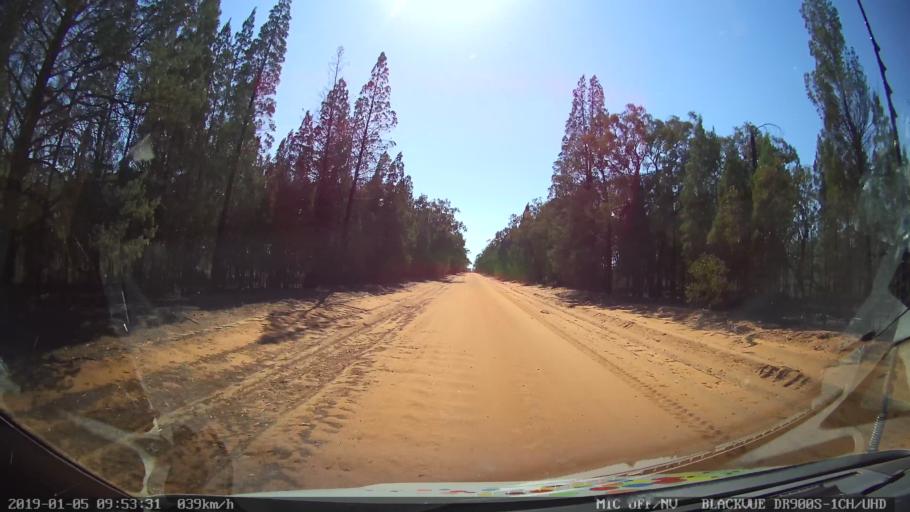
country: AU
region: New South Wales
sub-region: Gilgandra
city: Gilgandra
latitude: -31.6623
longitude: 148.7737
